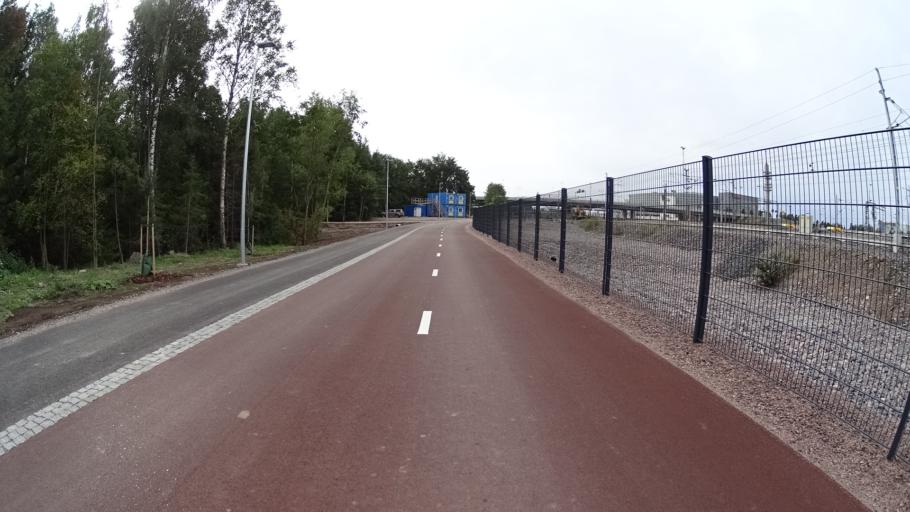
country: FI
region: Uusimaa
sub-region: Helsinki
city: Helsinki
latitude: 60.2086
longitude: 24.9345
